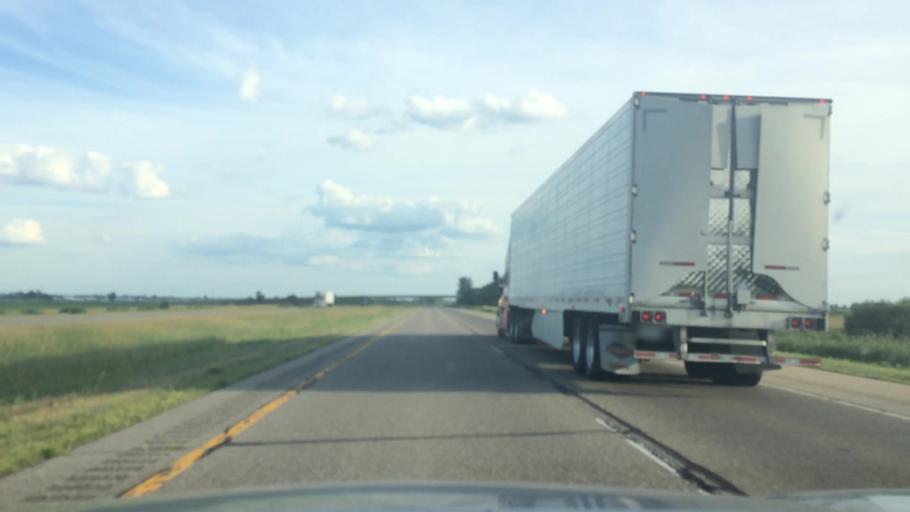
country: US
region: Wisconsin
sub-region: Portage County
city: Plover
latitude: 44.3731
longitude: -89.5200
